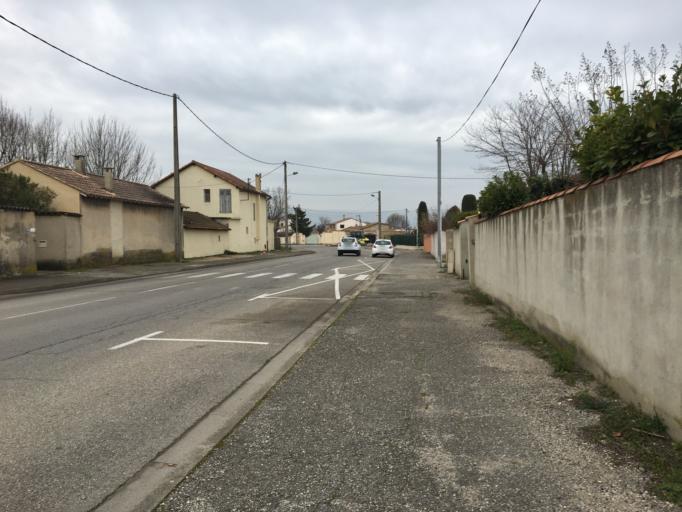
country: FR
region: Provence-Alpes-Cote d'Azur
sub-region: Departement du Vaucluse
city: Orange
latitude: 44.1351
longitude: 4.8269
